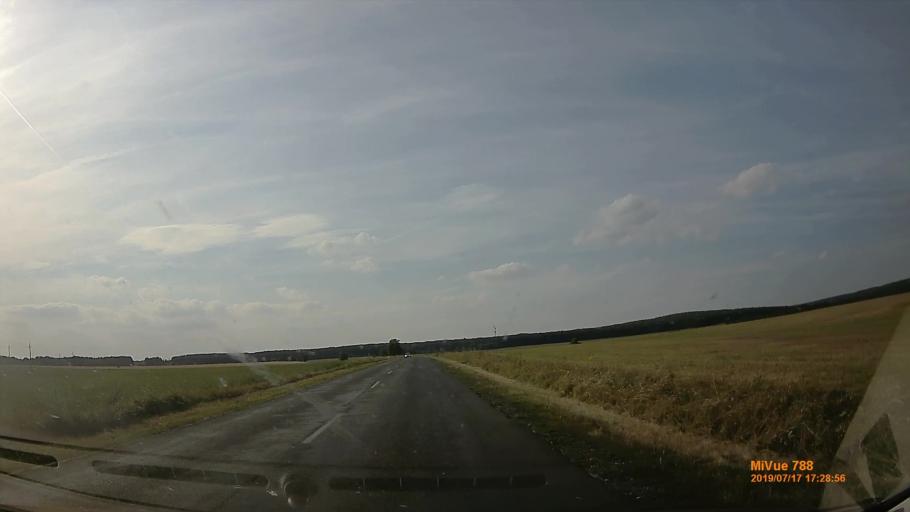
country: HU
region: Veszprem
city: Urkut
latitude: 47.0120
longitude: 17.5903
